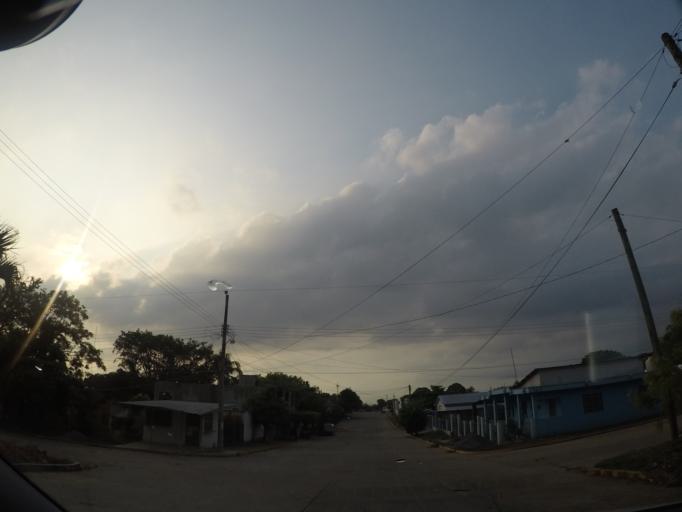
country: MX
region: Oaxaca
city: Matias Romero
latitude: 16.8716
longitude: -95.0400
